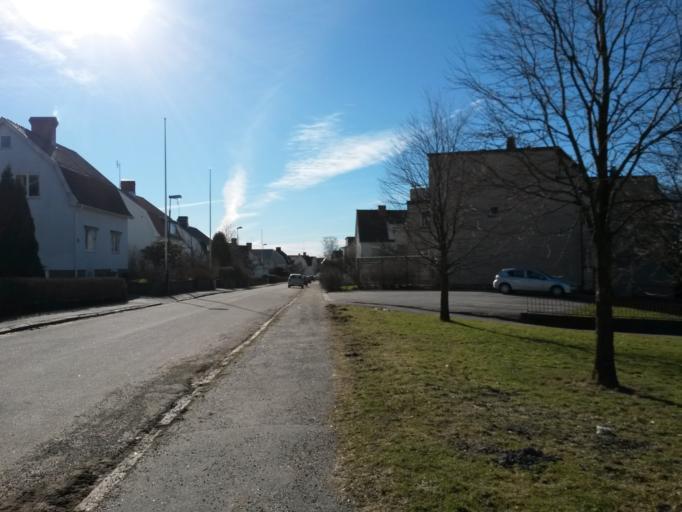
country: SE
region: Vaestra Goetaland
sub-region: Boras Kommun
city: Boras
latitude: 57.7322
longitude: 12.9477
